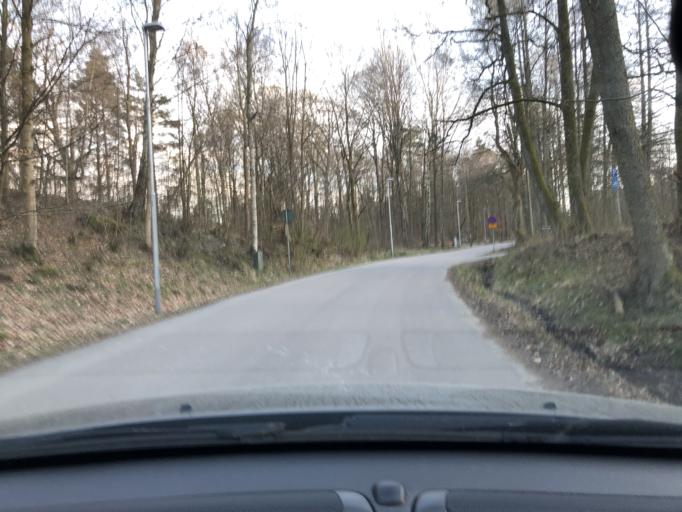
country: SE
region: Vaestra Goetaland
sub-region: Molndal
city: Moelndal
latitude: 57.6938
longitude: 12.0345
